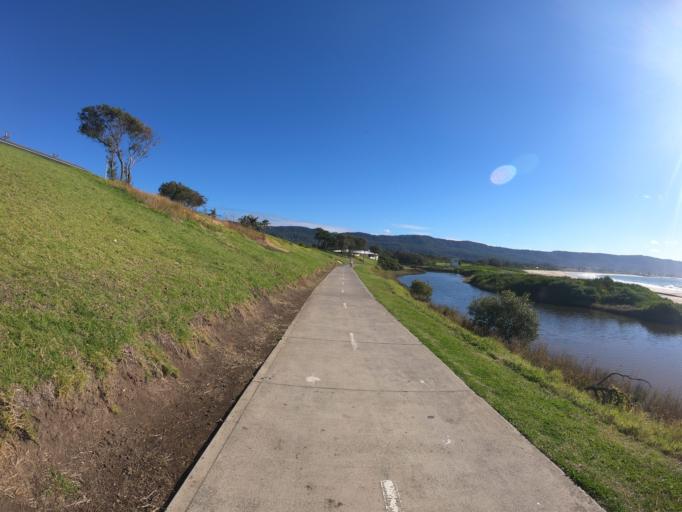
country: AU
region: New South Wales
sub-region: Wollongong
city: East Corrimal
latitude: -34.3654
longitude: 150.9215
